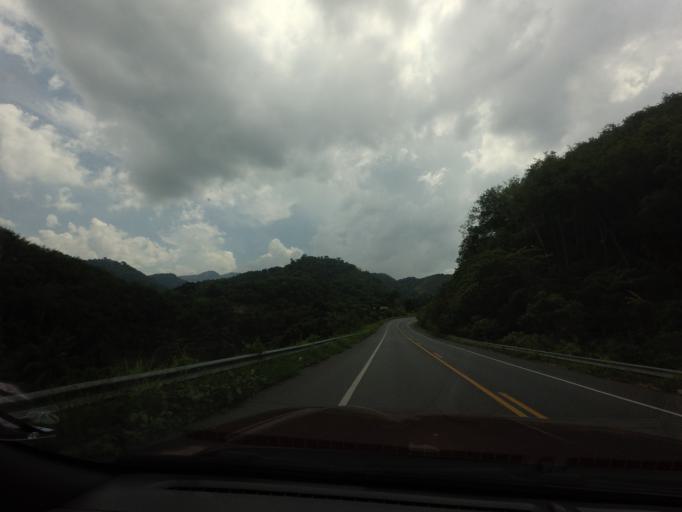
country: TH
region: Yala
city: Than To
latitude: 6.0535
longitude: 101.1941
